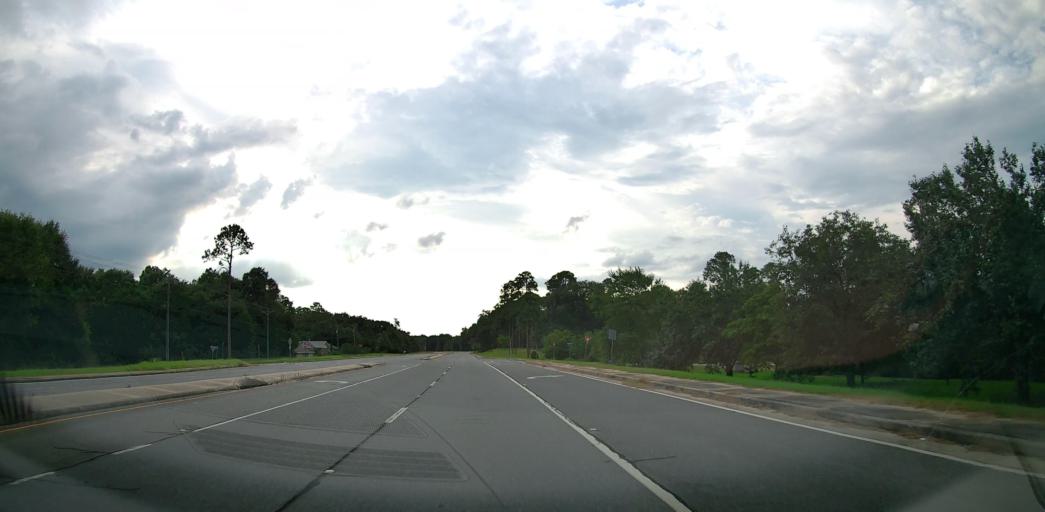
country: US
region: Georgia
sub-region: Pulaski County
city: Hawkinsville
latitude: 32.2791
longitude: -83.4288
